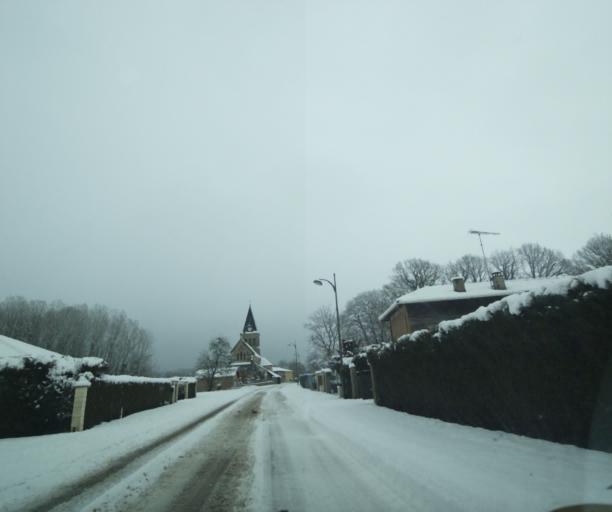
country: FR
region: Champagne-Ardenne
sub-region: Departement de la Haute-Marne
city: Montier-en-Der
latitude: 48.5358
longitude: 4.8135
